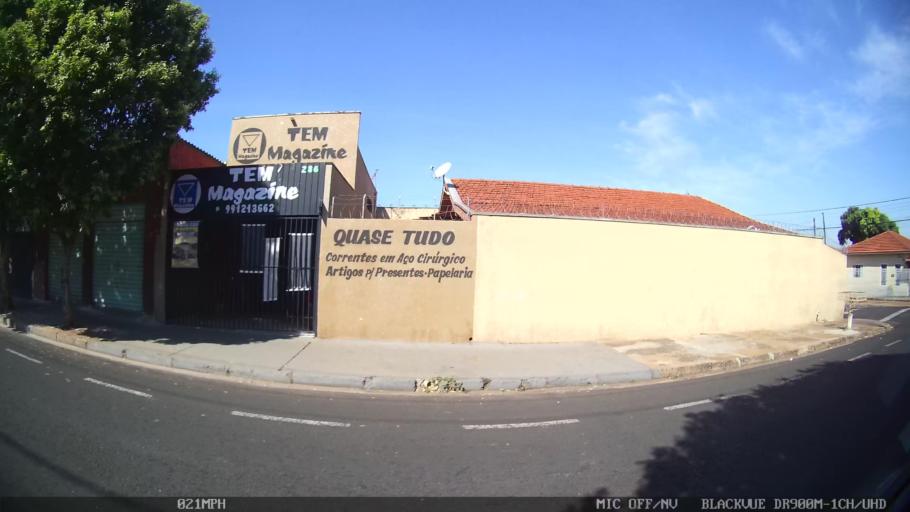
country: BR
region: Sao Paulo
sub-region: Sao Jose Do Rio Preto
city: Sao Jose do Rio Preto
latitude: -20.7818
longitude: -49.4098
